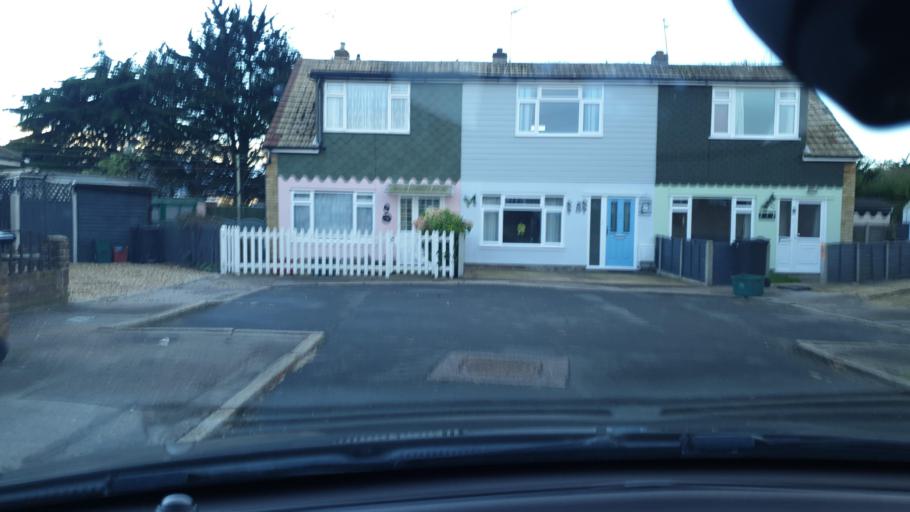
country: GB
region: England
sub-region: Essex
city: Clacton-on-Sea
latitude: 51.8083
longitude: 1.1703
